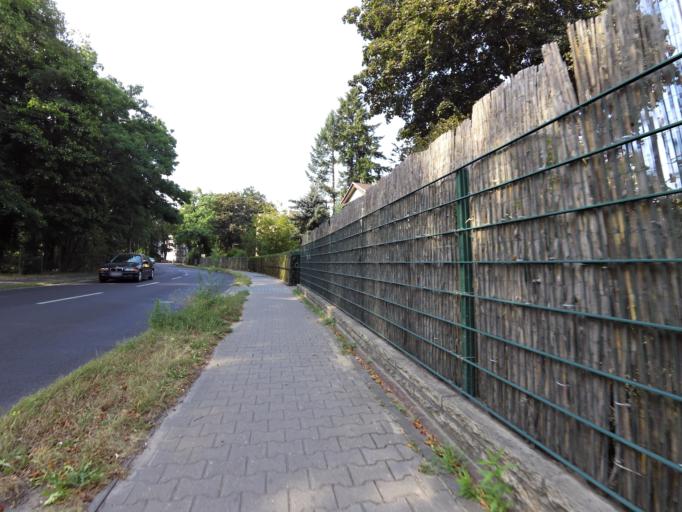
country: DE
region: Berlin
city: Grunau
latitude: 52.4100
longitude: 13.5731
